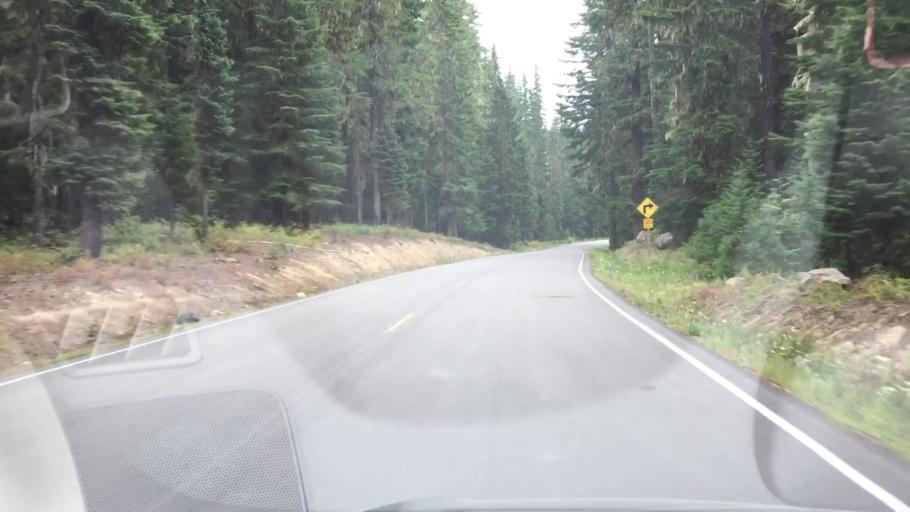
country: US
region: Washington
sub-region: Klickitat County
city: White Salmon
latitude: 46.1997
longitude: -121.6452
